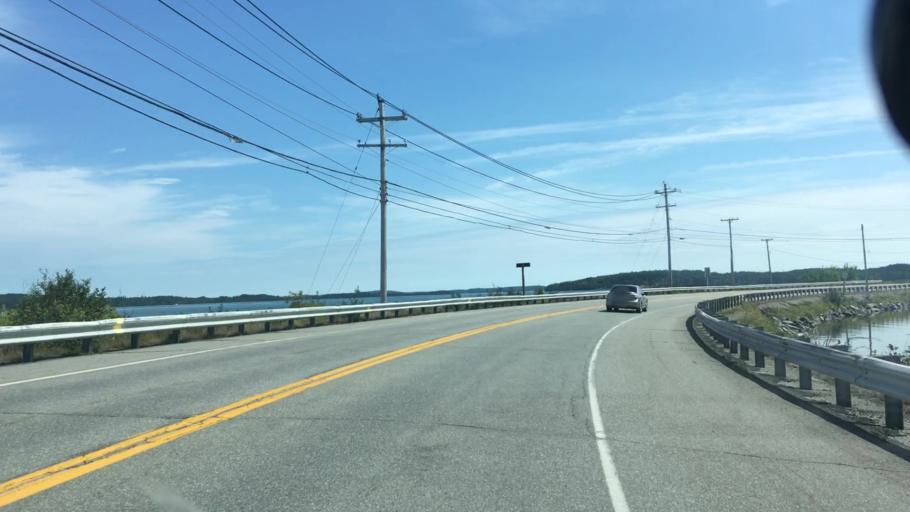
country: US
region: Maine
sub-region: Washington County
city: Eastport
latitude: 44.9545
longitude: -67.0403
